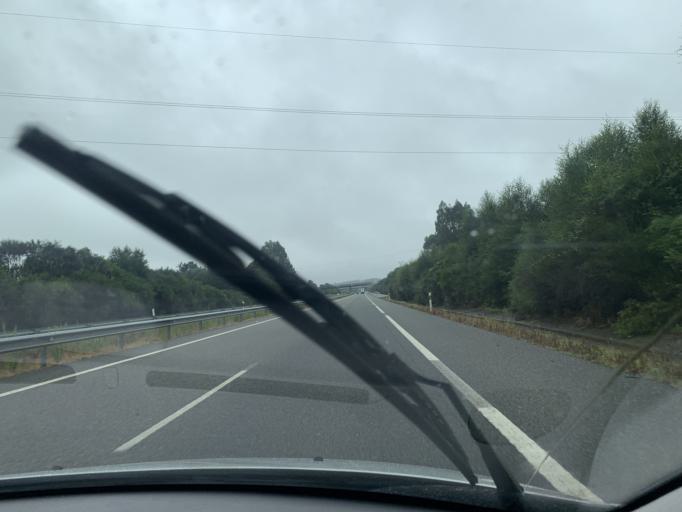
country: ES
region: Galicia
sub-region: Provincia de Lugo
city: Vilalba
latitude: 43.3218
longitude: -7.6674
